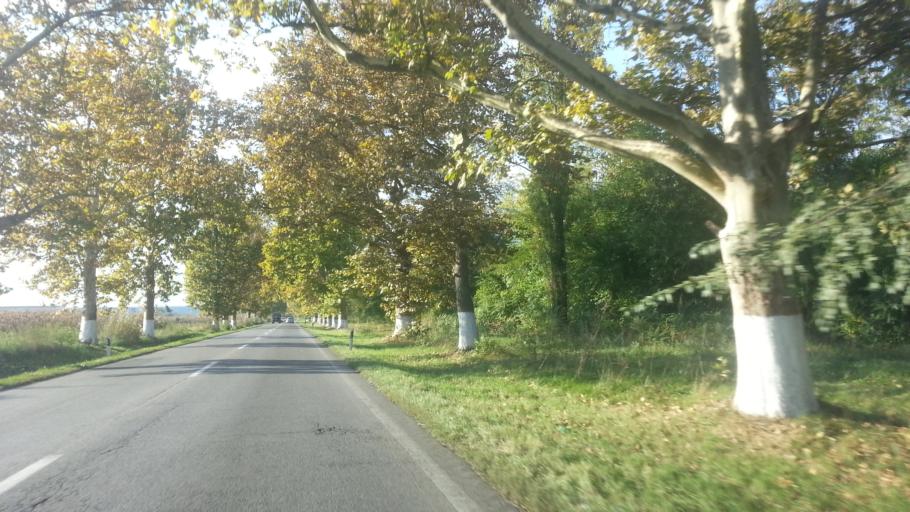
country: RS
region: Autonomna Pokrajina Vojvodina
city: Nova Pazova
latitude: 44.9326
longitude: 20.2363
